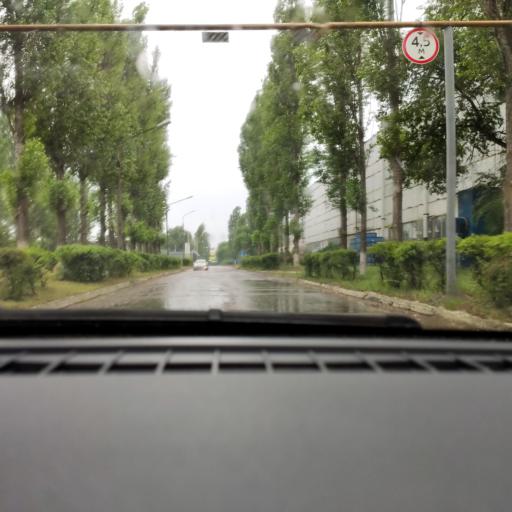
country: RU
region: Voronezj
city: Somovo
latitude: 51.7140
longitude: 39.2908
